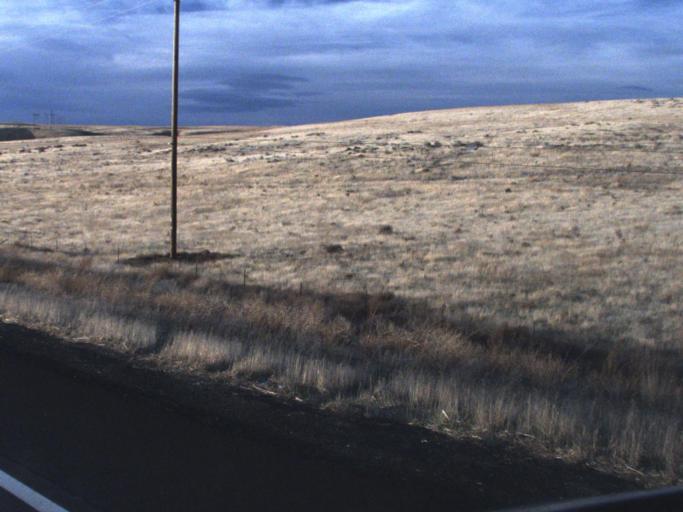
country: US
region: Washington
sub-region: Walla Walla County
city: Burbank
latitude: 46.0685
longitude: -118.7641
